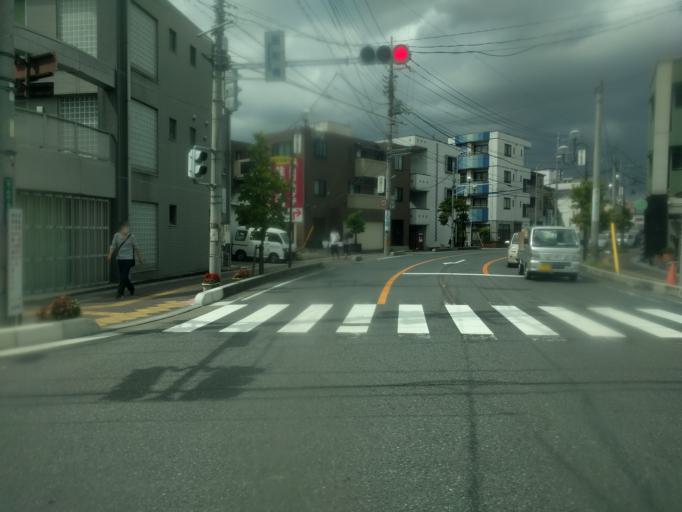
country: JP
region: Saitama
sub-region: Kawaguchi-shi
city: Hatogaya-honcho
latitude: 35.8302
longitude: 139.7392
